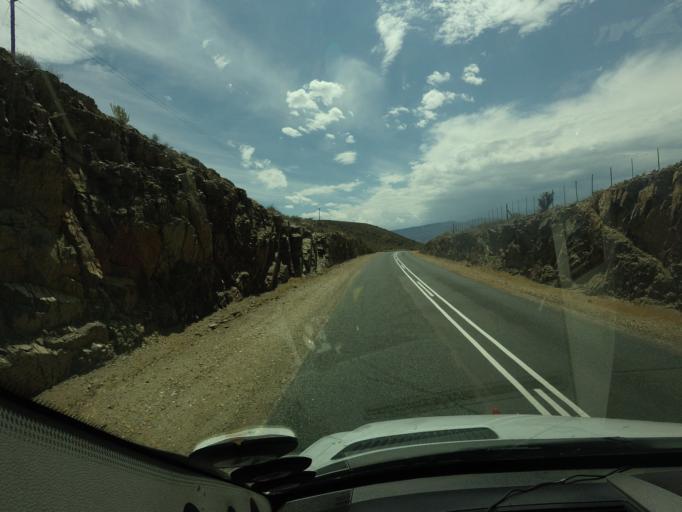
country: ZA
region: Western Cape
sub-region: Eden District Municipality
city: Ladismith
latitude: -33.7004
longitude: 20.9646
